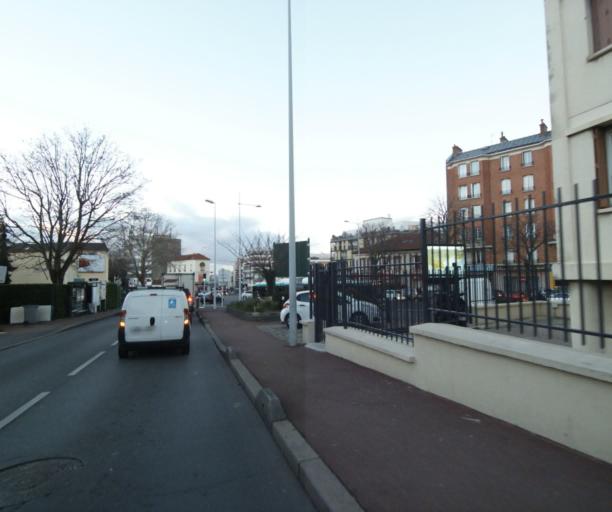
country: FR
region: Ile-de-France
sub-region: Departement des Hauts-de-Seine
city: Nanterre
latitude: 48.8860
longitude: 2.2101
